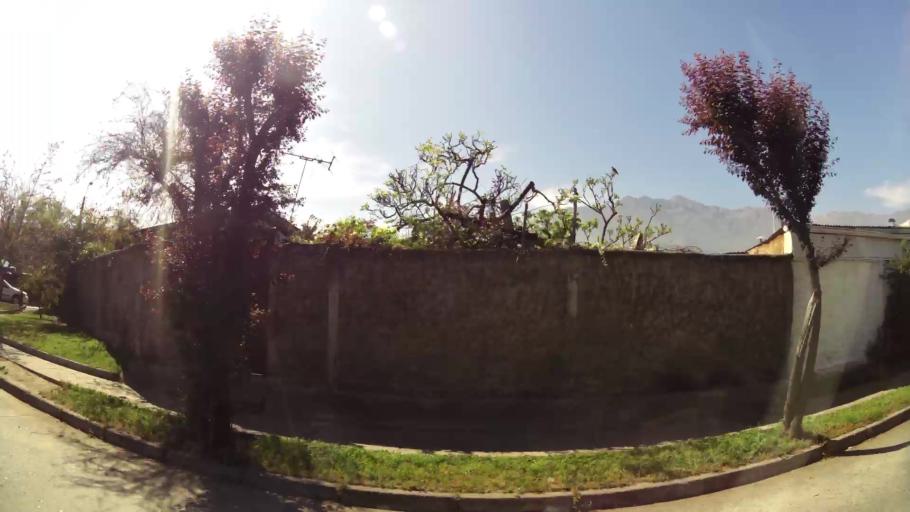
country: CL
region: Santiago Metropolitan
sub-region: Provincia de Santiago
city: Villa Presidente Frei, Nunoa, Santiago, Chile
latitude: -33.4476
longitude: -70.5406
